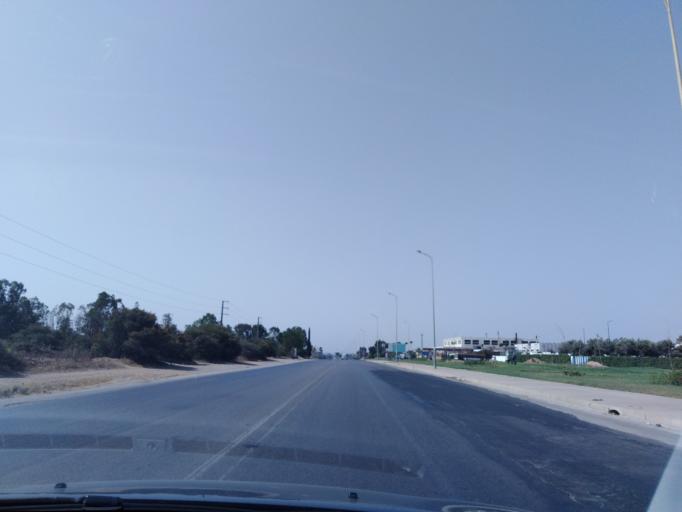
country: MA
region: Chaouia-Ouardigha
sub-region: Settat Province
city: Berrechid
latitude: 33.2491
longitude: -7.5852
